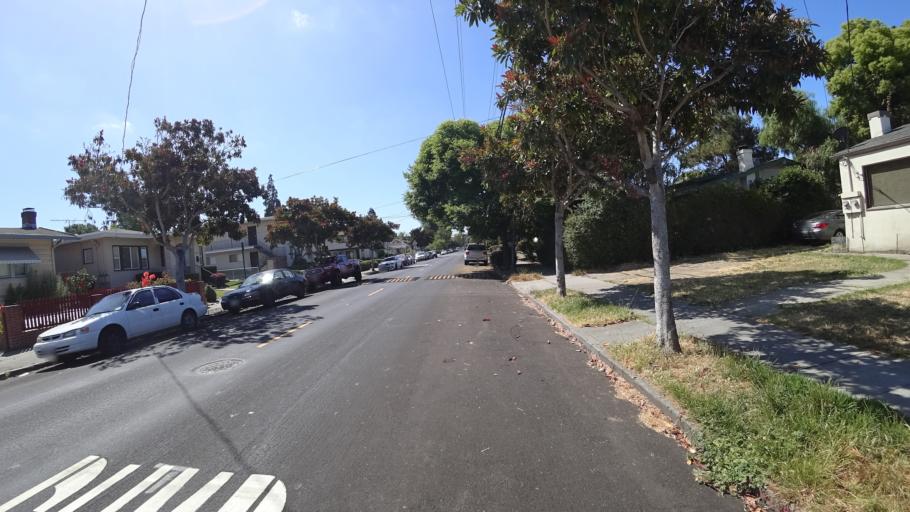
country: US
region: California
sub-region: Alameda County
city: Hayward
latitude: 37.6746
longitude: -122.0898
